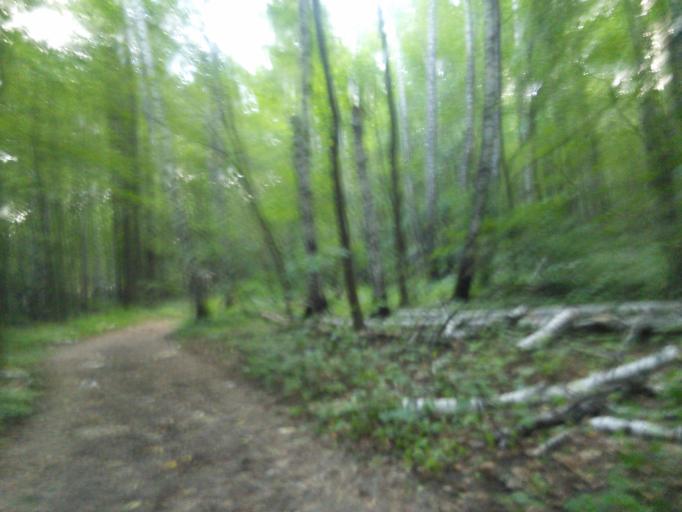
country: RU
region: Moscow
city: Sokol'niki
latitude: 55.8128
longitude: 37.6769
